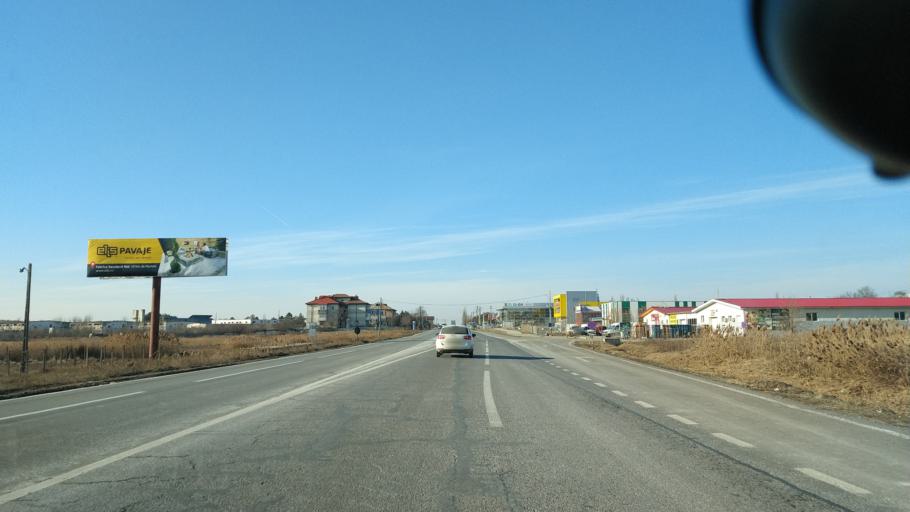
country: RO
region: Iasi
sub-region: Comuna Letcani
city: Letcani
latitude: 47.1845
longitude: 27.4562
